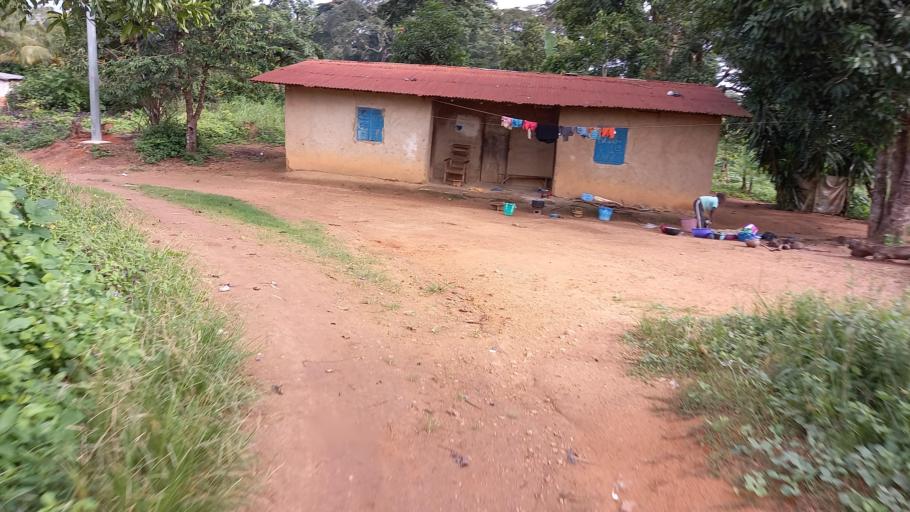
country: SL
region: Eastern Province
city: Kailahun
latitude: 8.2791
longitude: -10.5799
